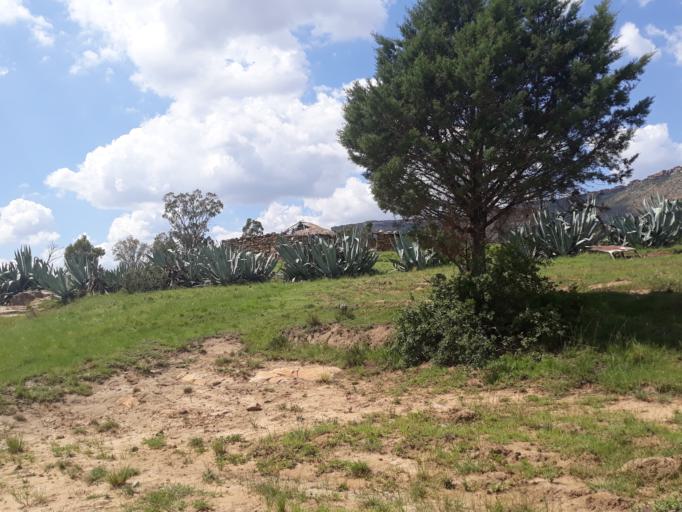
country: LS
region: Quthing
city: Quthing
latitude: -30.3419
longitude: 27.5277
